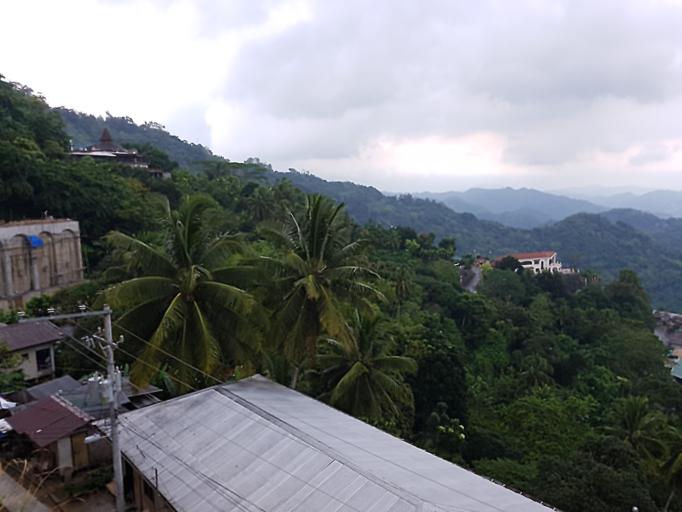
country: PH
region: Central Visayas
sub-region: Province of Cebu
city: Cebu City
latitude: 10.3689
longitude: 123.8736
